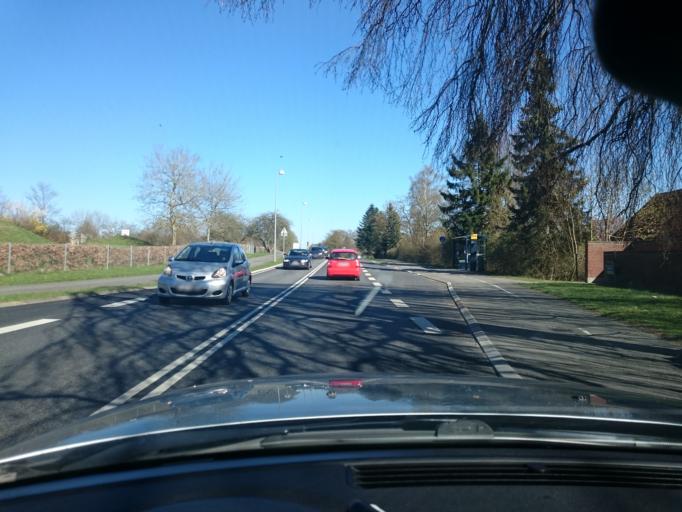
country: DK
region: Capital Region
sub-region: Fureso Kommune
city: Vaerlose
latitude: 55.7820
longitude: 12.3515
